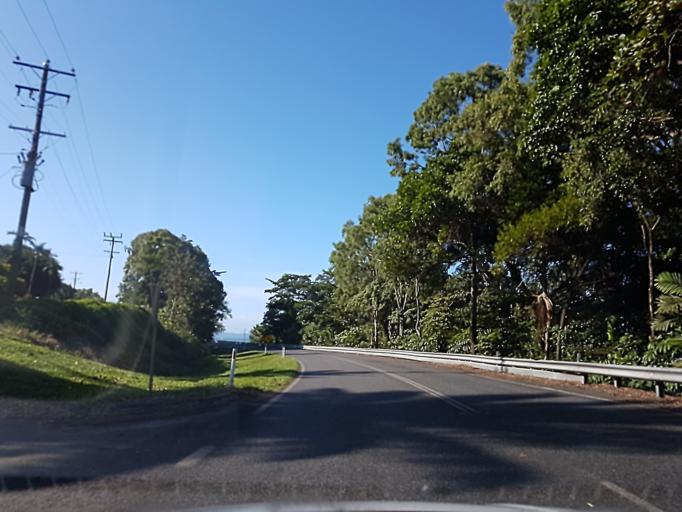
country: AU
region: Queensland
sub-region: Cairns
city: Port Douglas
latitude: -16.3895
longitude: 145.4177
